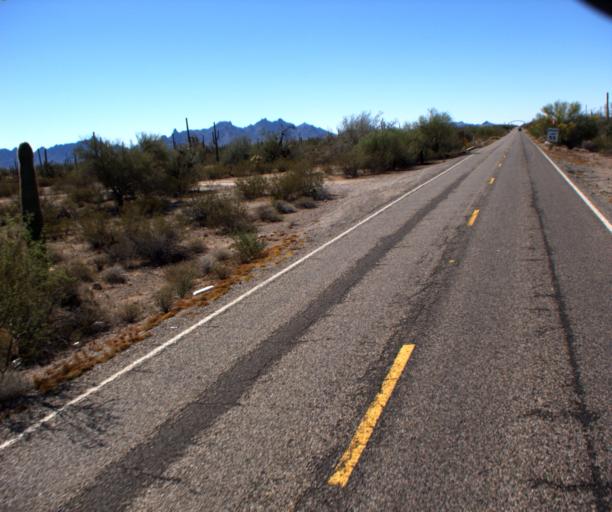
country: US
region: Arizona
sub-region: Pima County
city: Ajo
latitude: 32.2089
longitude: -112.7584
